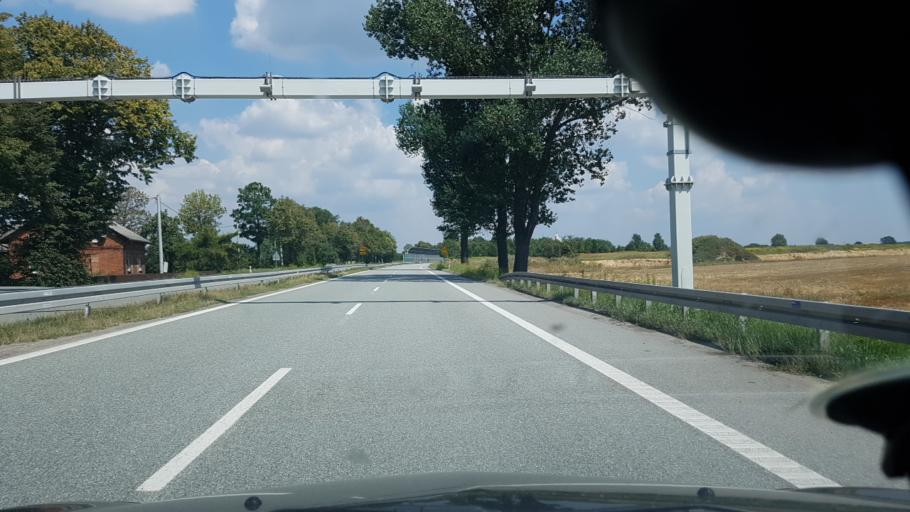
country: PL
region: Silesian Voivodeship
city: Gardawice
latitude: 50.1028
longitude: 18.7809
